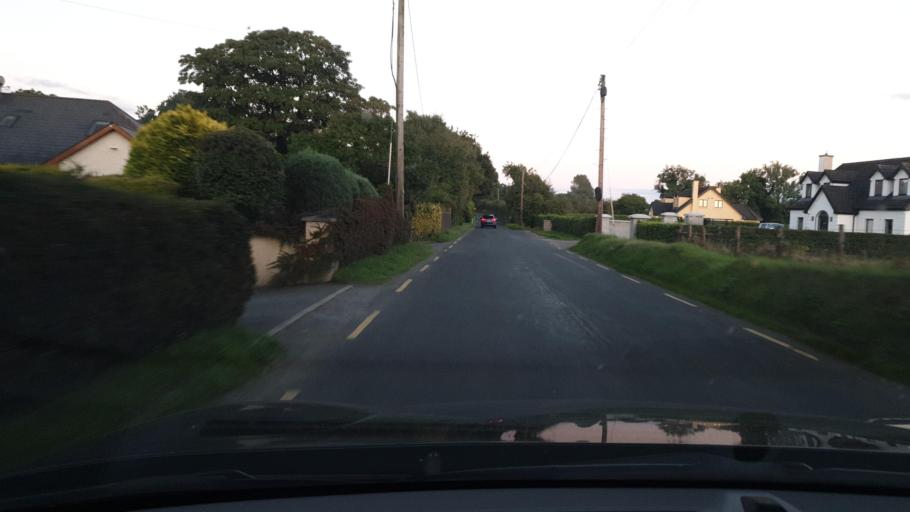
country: IE
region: Leinster
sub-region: Kildare
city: Clane
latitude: 53.3415
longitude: -6.7217
